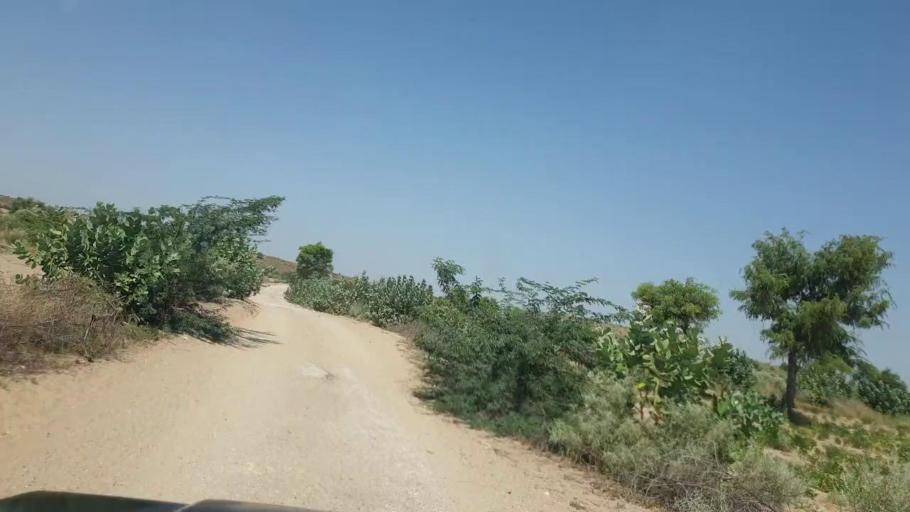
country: PK
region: Sindh
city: Chor
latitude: 25.3816
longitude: 70.3138
